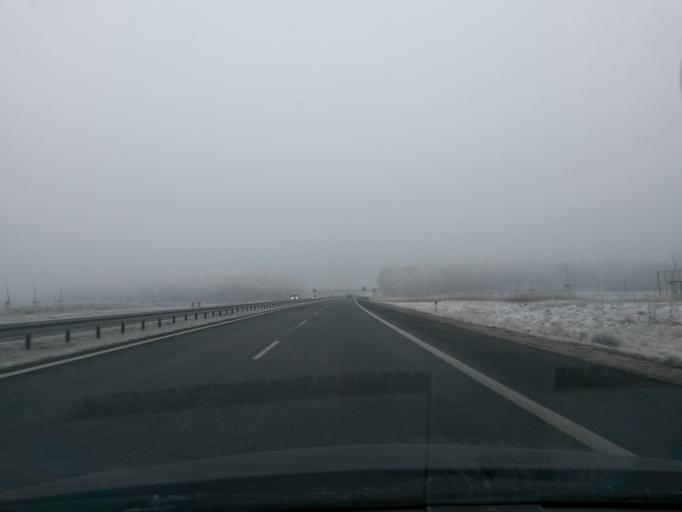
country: PL
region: Greater Poland Voivodeship
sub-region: Powiat poznanski
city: Pobiedziska
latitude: 52.4270
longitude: 17.3142
